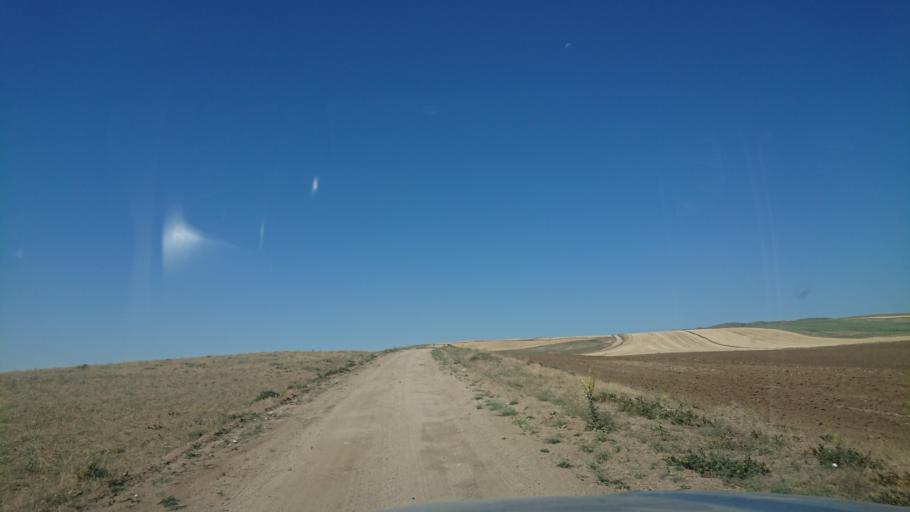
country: TR
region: Aksaray
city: Sariyahsi
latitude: 38.9281
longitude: 33.8544
